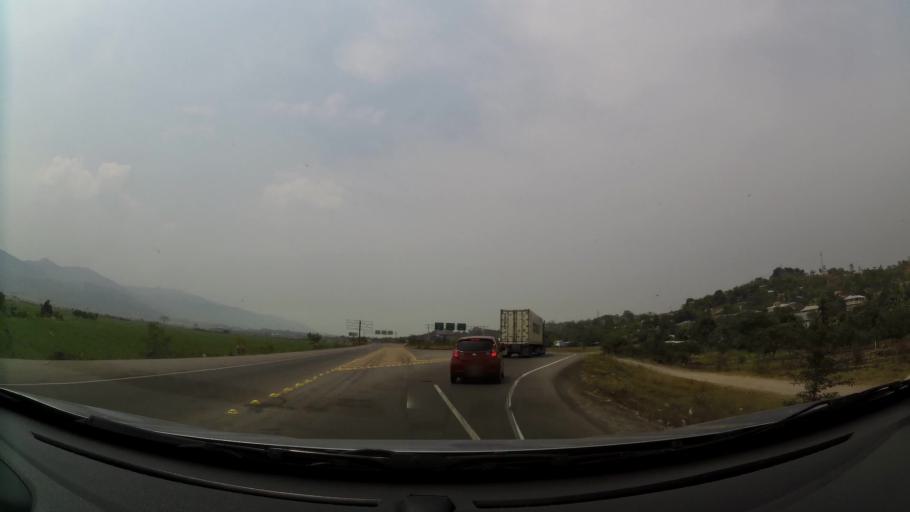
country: HN
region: Cortes
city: El Plan
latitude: 15.2834
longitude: -87.9775
